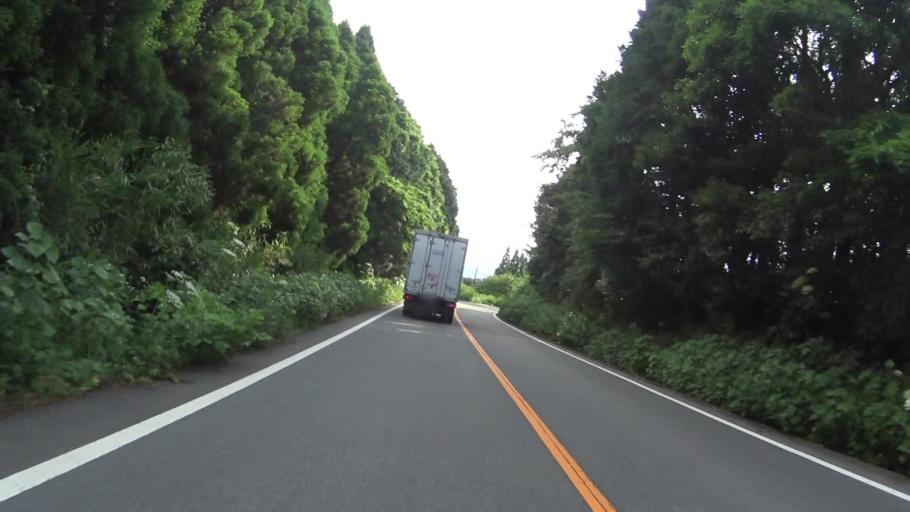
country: JP
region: Kumamoto
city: Aso
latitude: 32.8998
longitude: 131.0147
